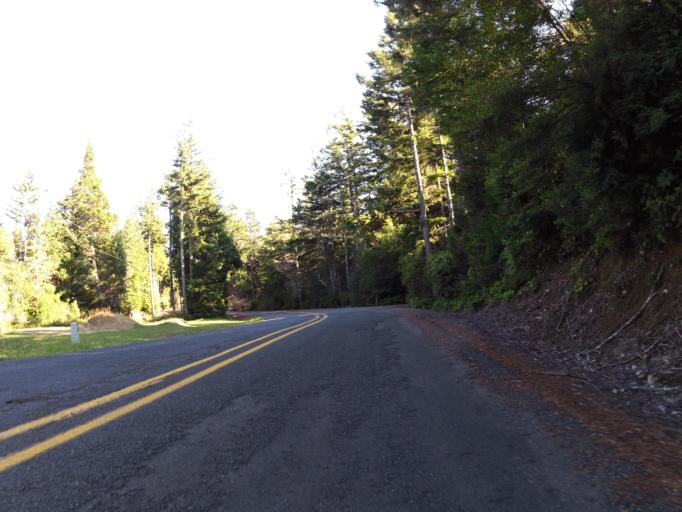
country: US
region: Oregon
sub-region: Coos County
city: Bandon
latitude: 43.0382
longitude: -124.3964
